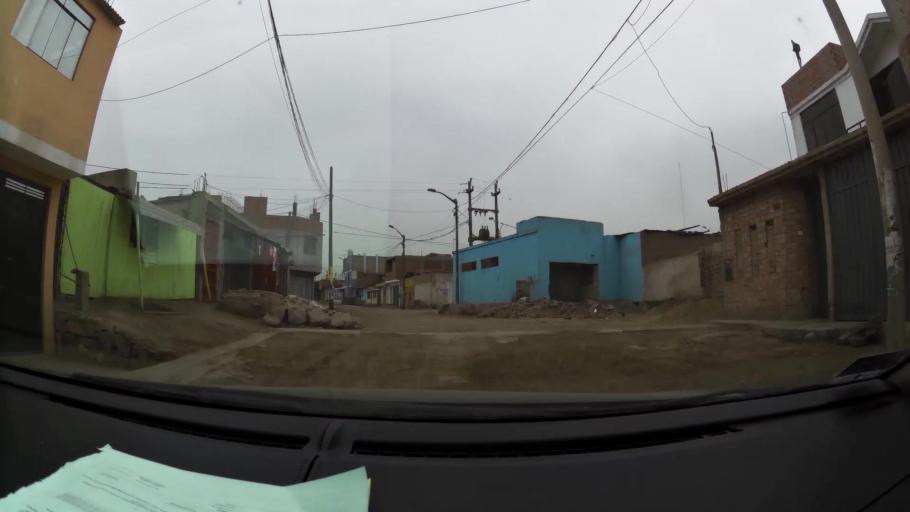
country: PE
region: Lima
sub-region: Lima
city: Urb. Santo Domingo
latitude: -11.9006
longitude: -77.0654
